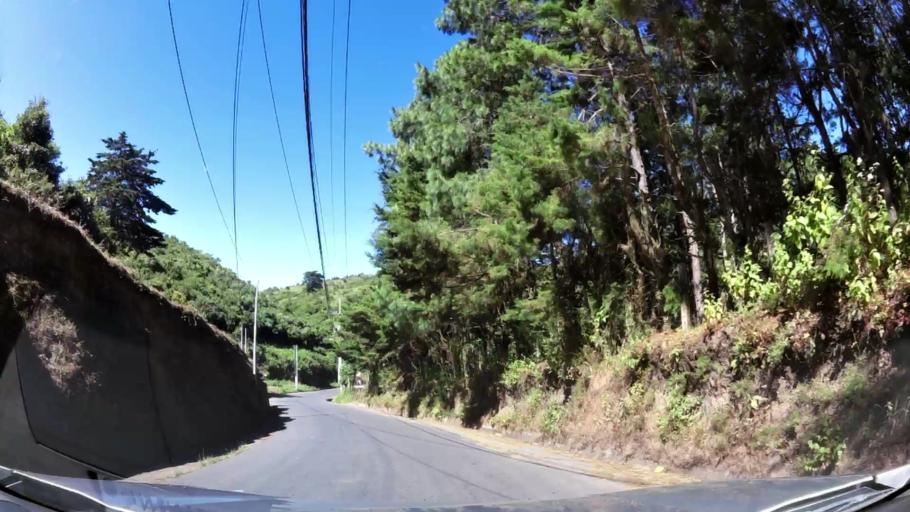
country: GT
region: Guatemala
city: San Jose Pinula
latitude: 14.5153
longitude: -90.4242
